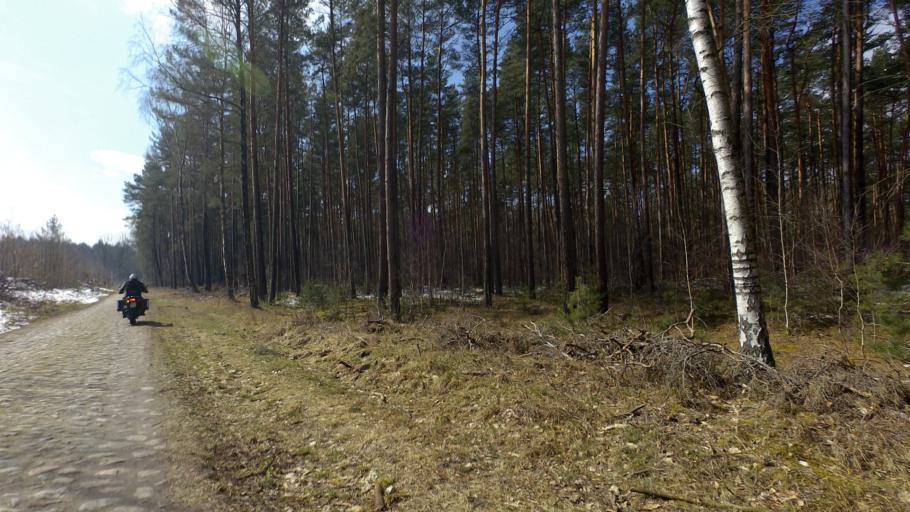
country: DE
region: Brandenburg
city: Werftpfuhl
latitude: 52.7077
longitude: 13.7861
